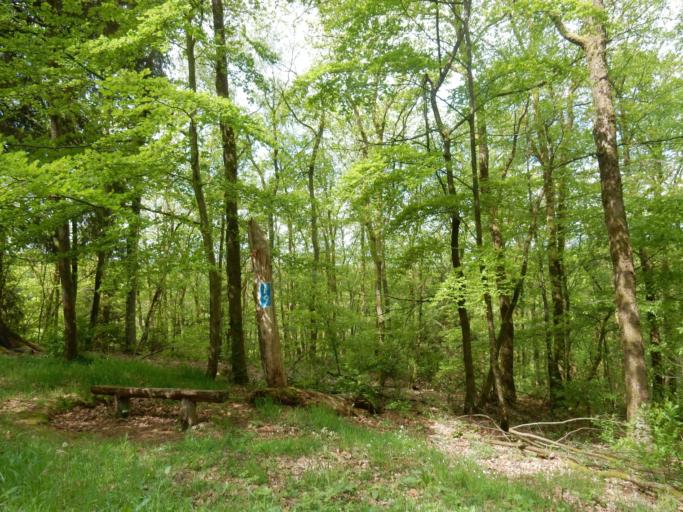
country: BE
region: Wallonia
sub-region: Province du Luxembourg
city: Bouillon
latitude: 49.7894
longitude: 5.0481
